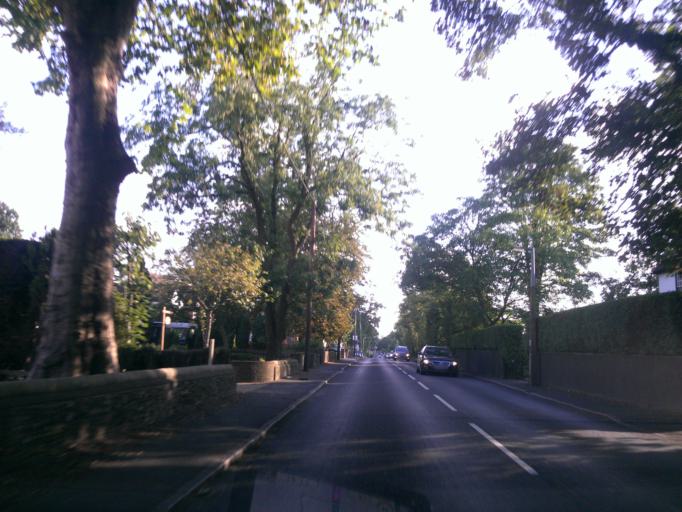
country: GB
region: England
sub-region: Essex
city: Braintree
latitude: 51.9119
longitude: 0.5792
